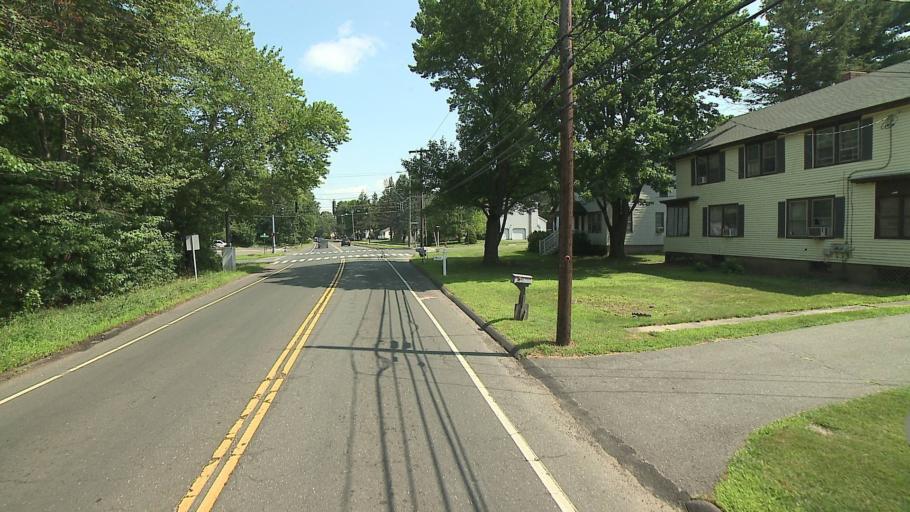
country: US
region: Connecticut
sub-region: Hartford County
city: Farmington
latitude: 41.7450
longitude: -72.8885
